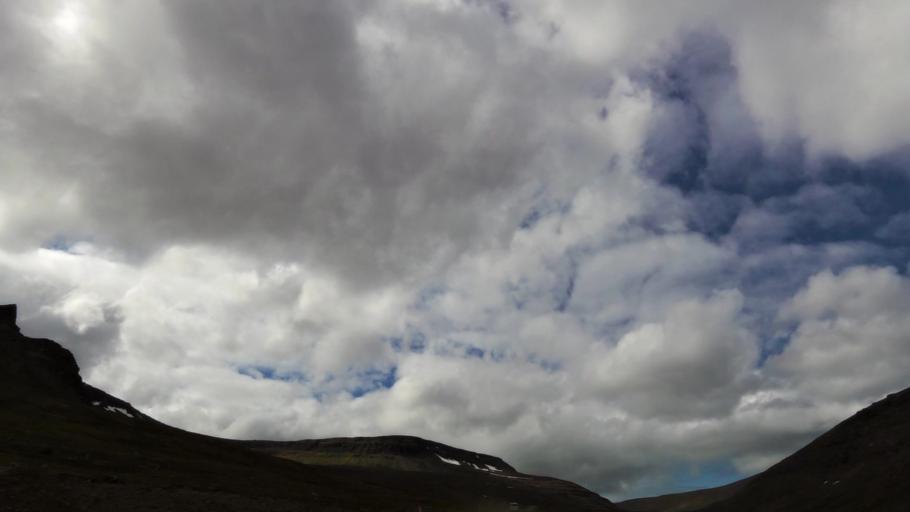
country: IS
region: Westfjords
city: Isafjoerdur
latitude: 66.1619
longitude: -23.3101
